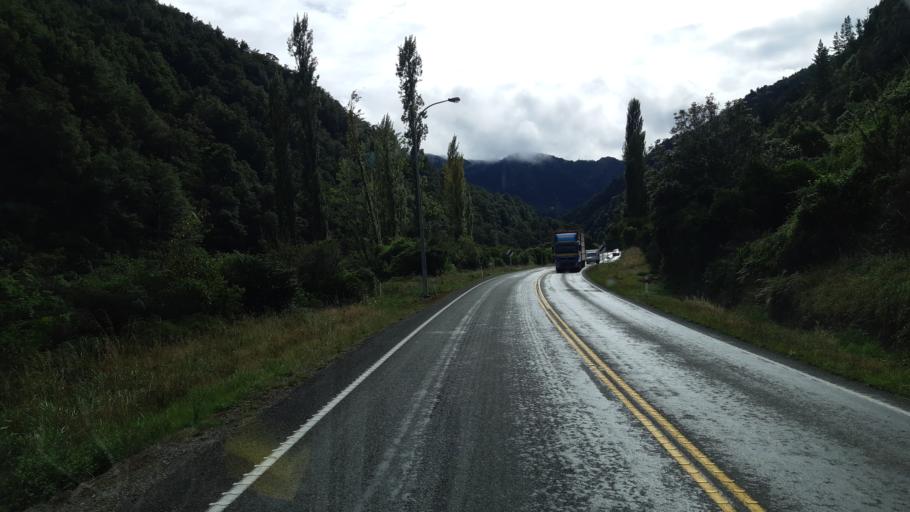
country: NZ
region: West Coast
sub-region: Buller District
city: Westport
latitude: -41.7770
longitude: 172.2201
